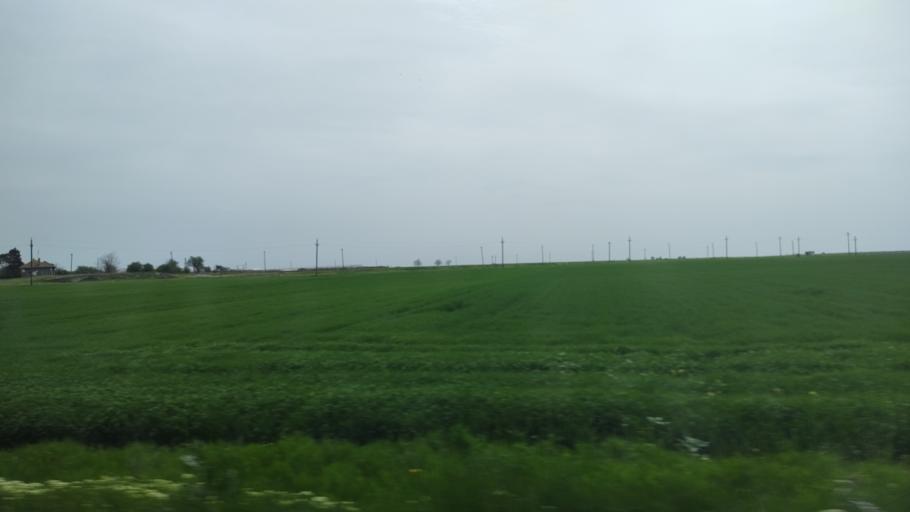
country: RO
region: Constanta
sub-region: Comuna Ciocarlia
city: Ciocarlia
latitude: 44.1002
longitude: 28.2747
